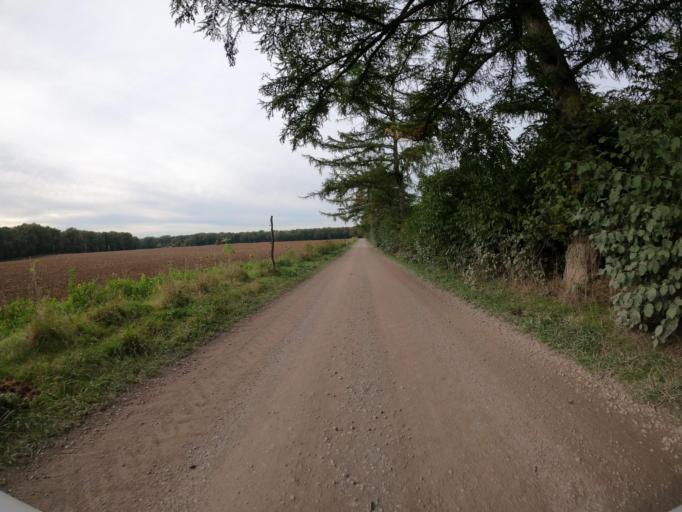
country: DE
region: North Rhine-Westphalia
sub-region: Regierungsbezirk Dusseldorf
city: Schermbeck
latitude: 51.7048
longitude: 6.8949
